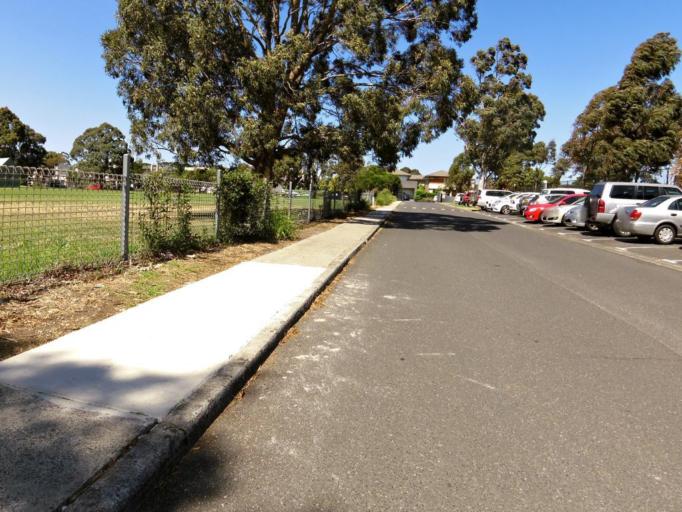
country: AU
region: Victoria
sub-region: Whitehorse
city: Blackburn South
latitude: -37.8484
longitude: 145.1629
